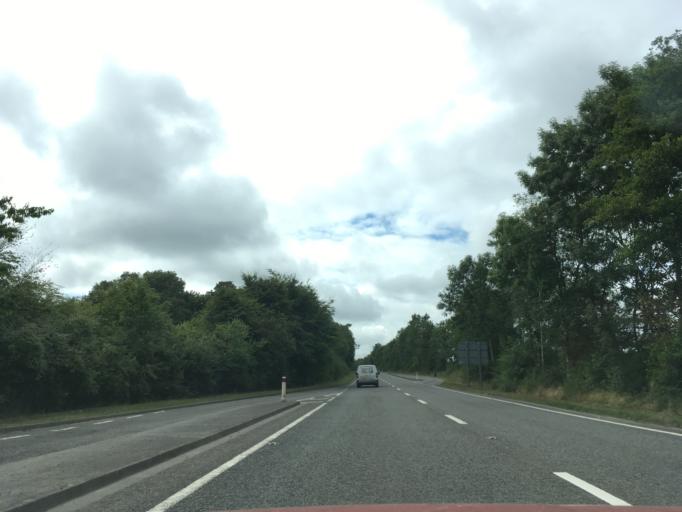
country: GB
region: Wales
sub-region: Carmarthenshire
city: Llandeilo
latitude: 51.8899
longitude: -3.9938
